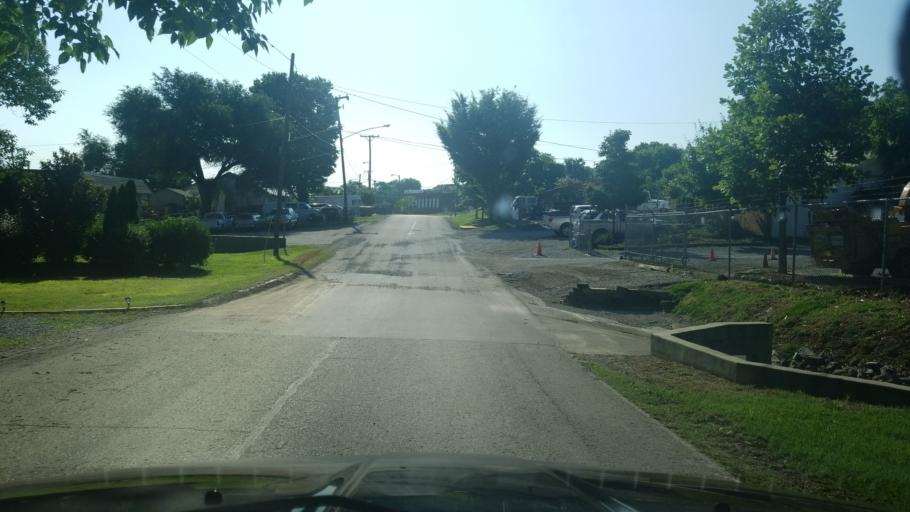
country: US
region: Tennessee
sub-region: Davidson County
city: Oak Hill
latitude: 36.1087
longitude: -86.7470
